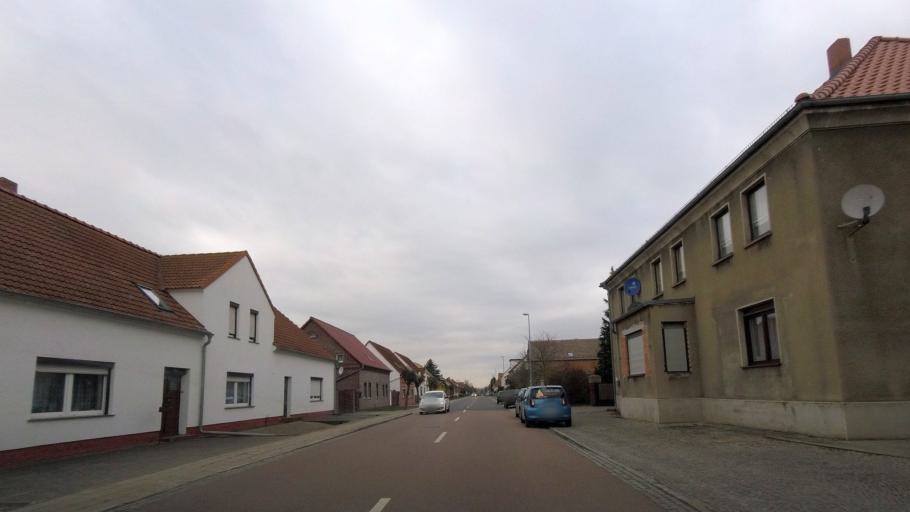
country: DE
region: Saxony-Anhalt
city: Bergwitz
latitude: 51.7958
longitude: 12.5871
